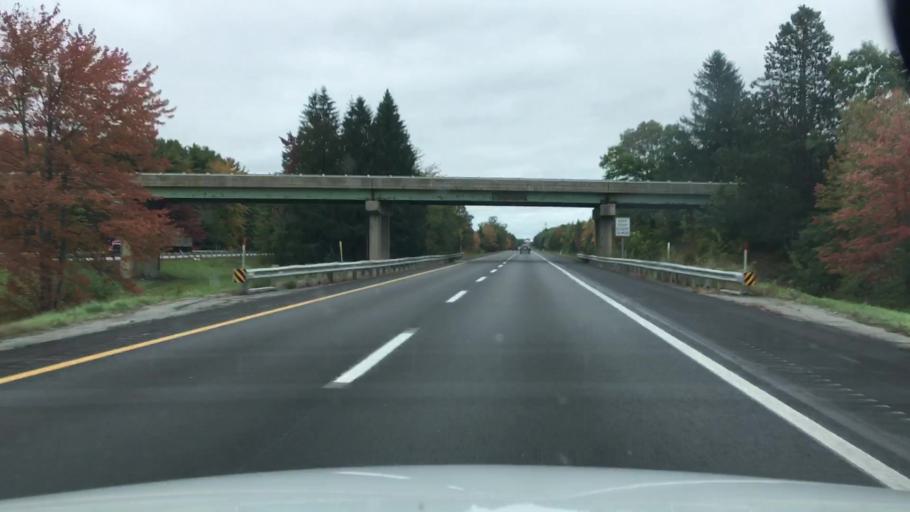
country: US
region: Maine
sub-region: Penobscot County
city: Veazie
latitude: 44.8455
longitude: -68.7307
